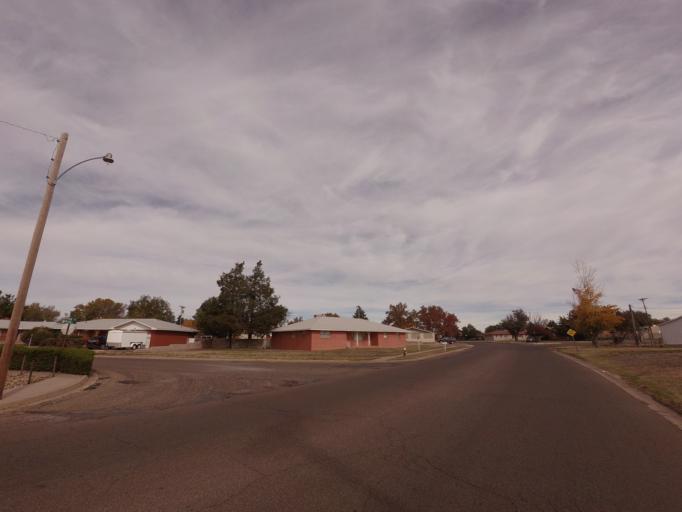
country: US
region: New Mexico
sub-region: Curry County
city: Clovis
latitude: 34.4220
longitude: -103.2074
